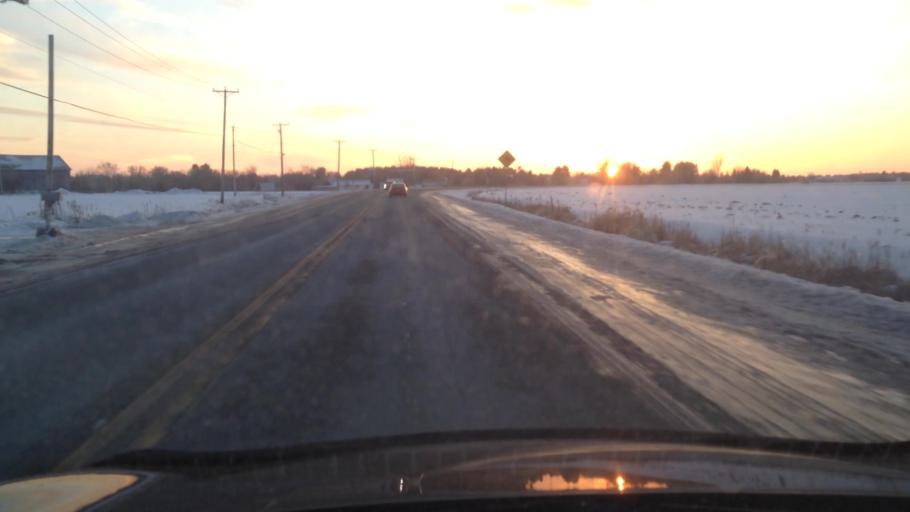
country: CA
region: Quebec
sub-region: Lanaudiere
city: Saint-Lin-Laurentides
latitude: 45.8484
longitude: -73.7886
